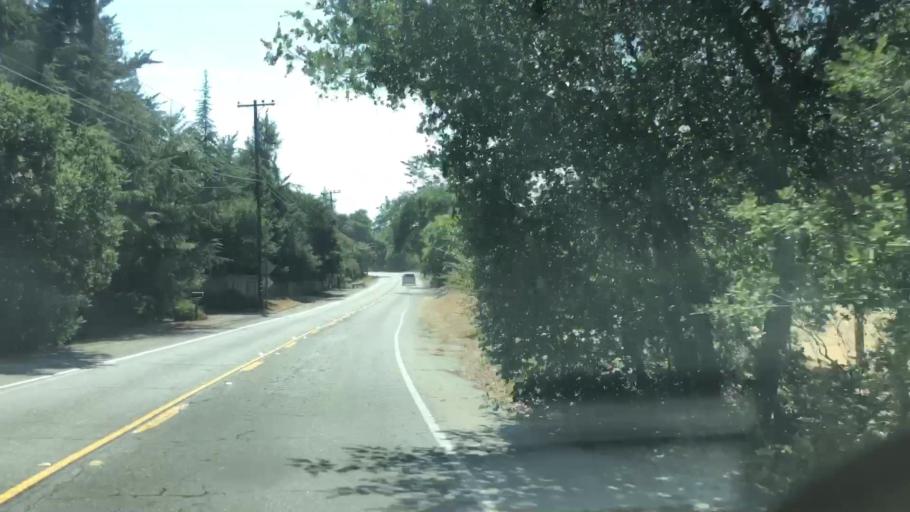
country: US
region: California
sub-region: Santa Cruz County
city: Corralitos
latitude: 36.9910
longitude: -121.8234
